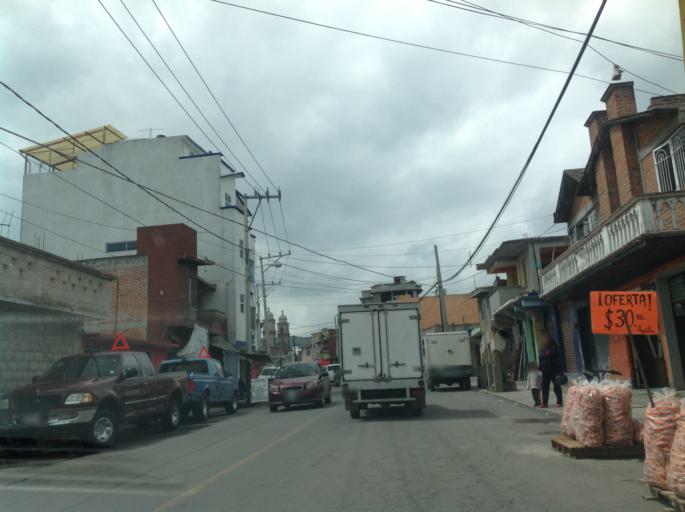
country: MX
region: Mexico
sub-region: Tenango del Valle
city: Santa Maria Jajalpa
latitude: 19.1141
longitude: -99.5375
